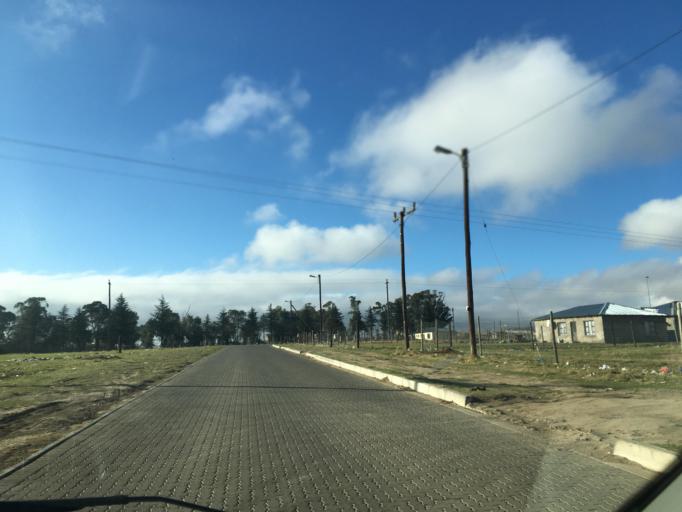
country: ZA
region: Eastern Cape
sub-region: Chris Hani District Municipality
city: Elliot
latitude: -31.3347
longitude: 27.8349
